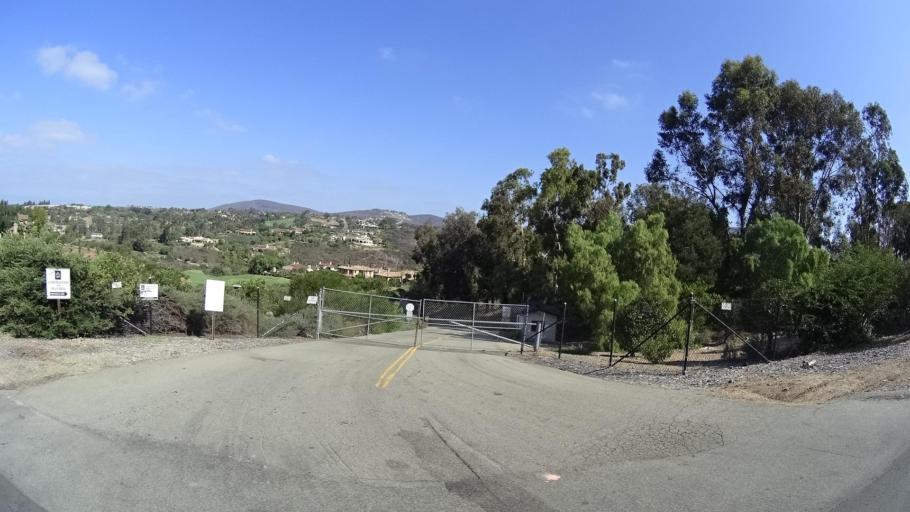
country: US
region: California
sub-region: San Diego County
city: Rancho Santa Fe
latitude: 33.0511
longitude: -117.1958
